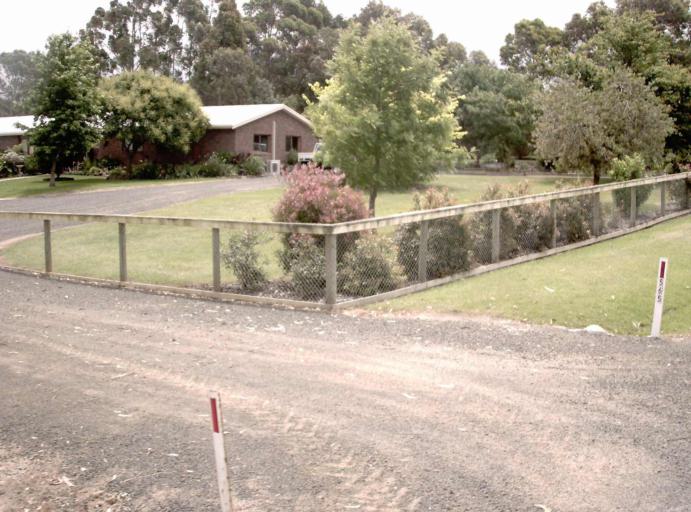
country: AU
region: Victoria
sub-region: Latrobe
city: Traralgon
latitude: -38.5218
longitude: 146.6606
